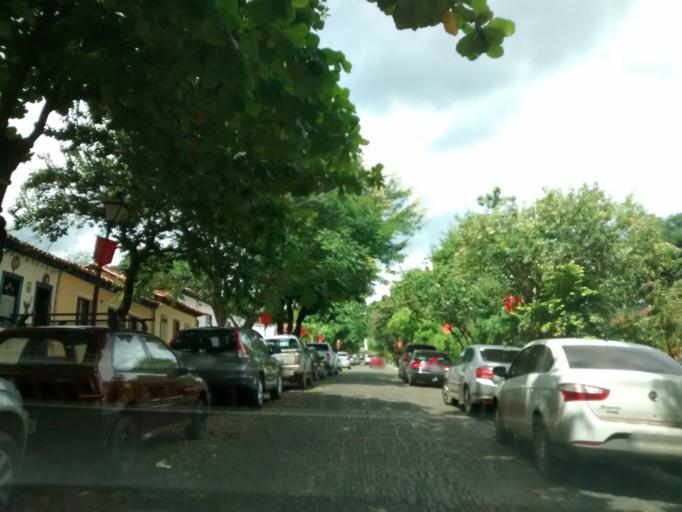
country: BR
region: Goias
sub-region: Pirenopolis
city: Pirenopolis
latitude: -15.8514
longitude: -48.9554
